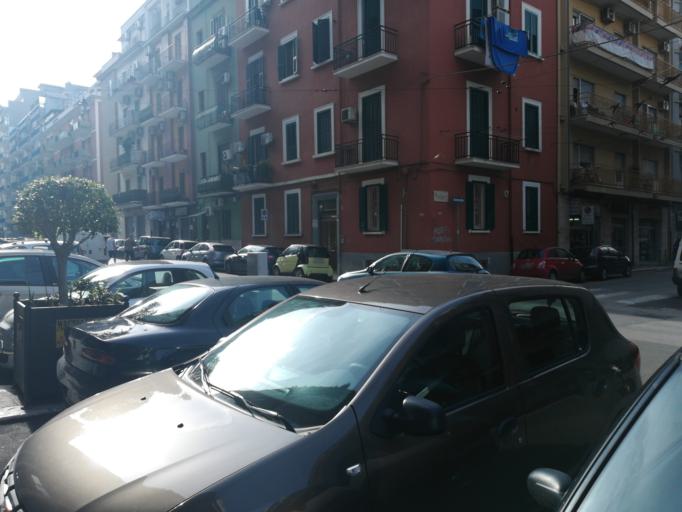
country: IT
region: Apulia
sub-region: Provincia di Bari
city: Bari
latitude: 41.1148
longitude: 16.8790
